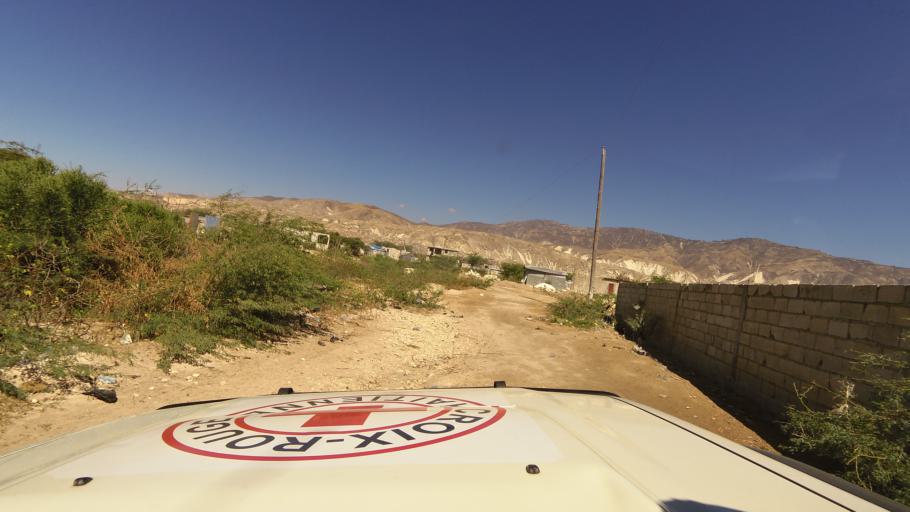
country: HT
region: Ouest
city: Croix des Bouquets
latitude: 18.6507
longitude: -72.2552
